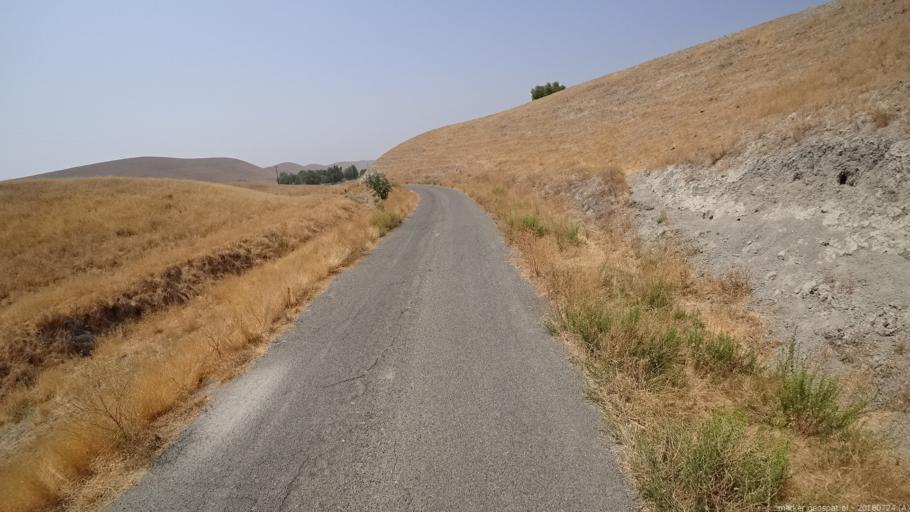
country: US
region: California
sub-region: Monterey County
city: King City
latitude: 36.1925
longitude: -120.9576
